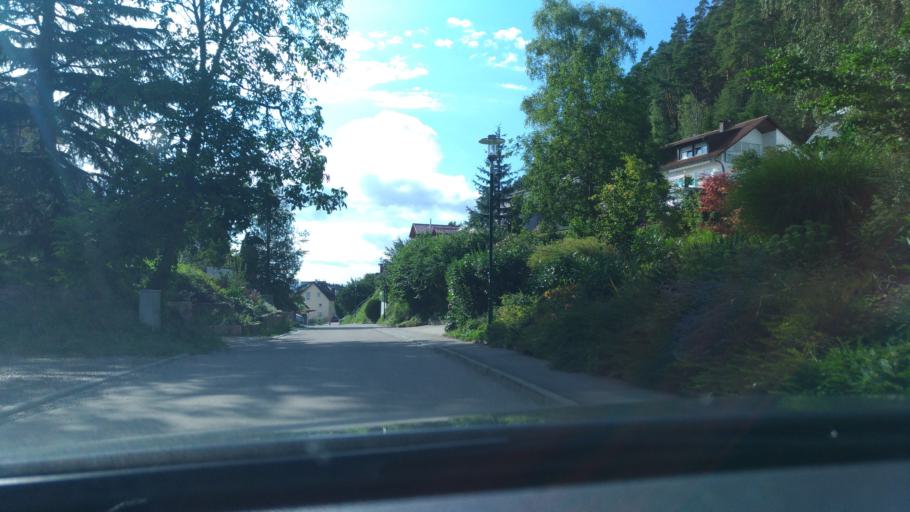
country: DE
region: Baden-Wuerttemberg
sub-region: Tuebingen Region
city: Sipplingen
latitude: 47.7955
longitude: 9.1052
